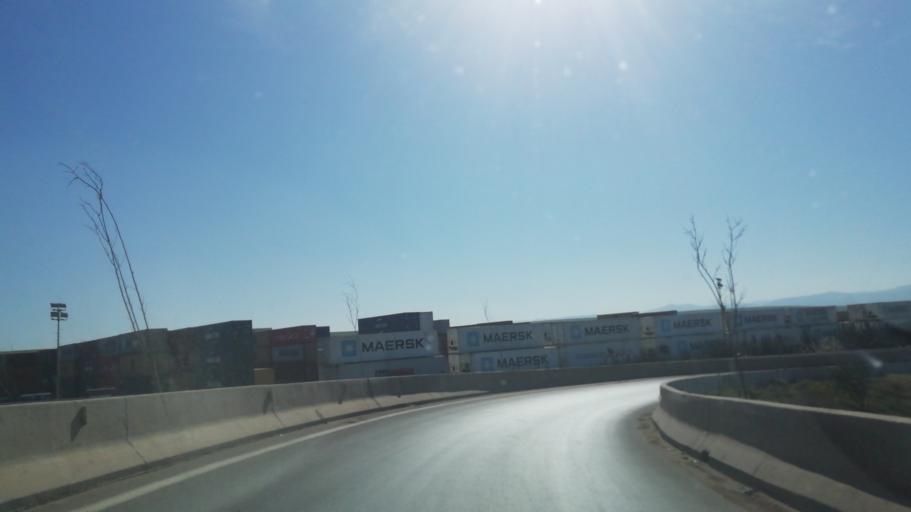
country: DZ
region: Oran
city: Es Senia
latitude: 35.6014
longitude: -0.5731
